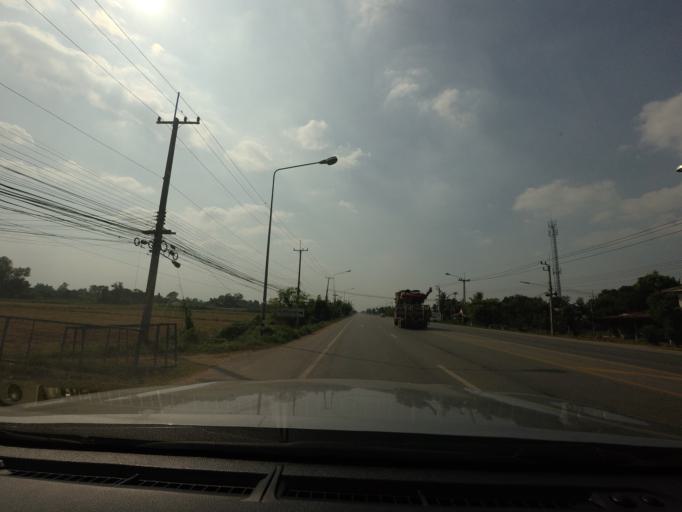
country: TH
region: Phitsanulok
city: Bang Rakam
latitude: 16.7726
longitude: 100.1689
